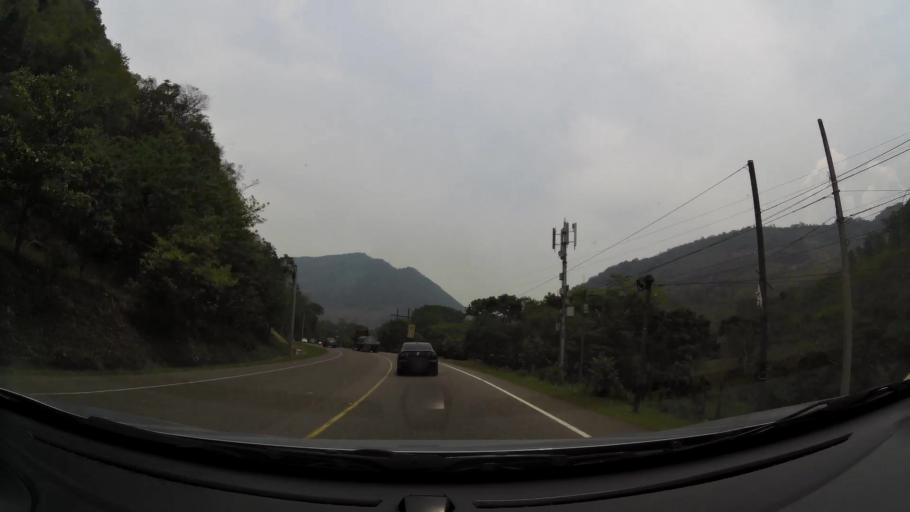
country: HN
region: Comayagua
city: Taulabe
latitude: 14.7296
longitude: -87.9633
